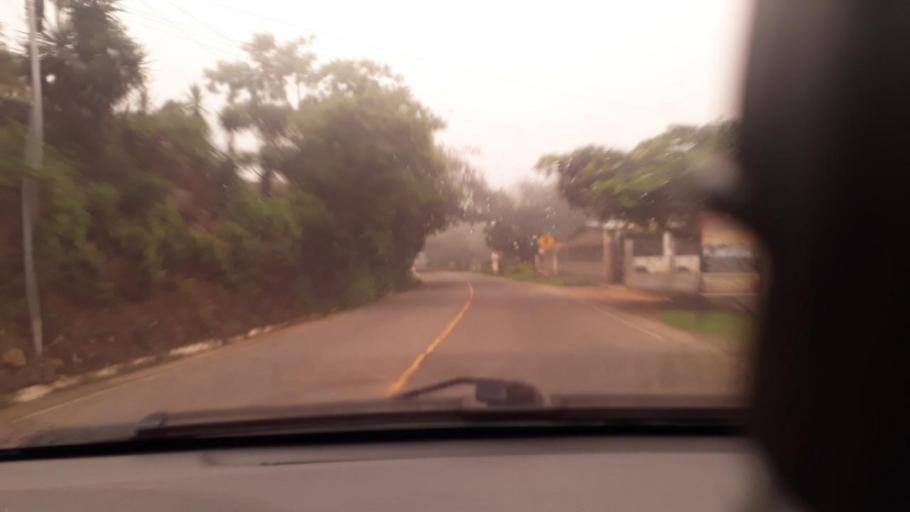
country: GT
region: Jutiapa
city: Jalpatagua
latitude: 14.1896
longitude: -90.0218
